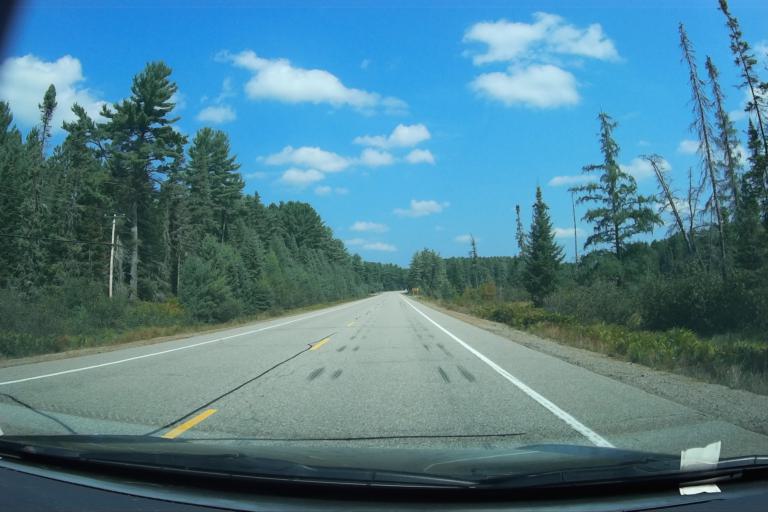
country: CA
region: Ontario
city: Huntsville
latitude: 45.5742
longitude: -78.5253
